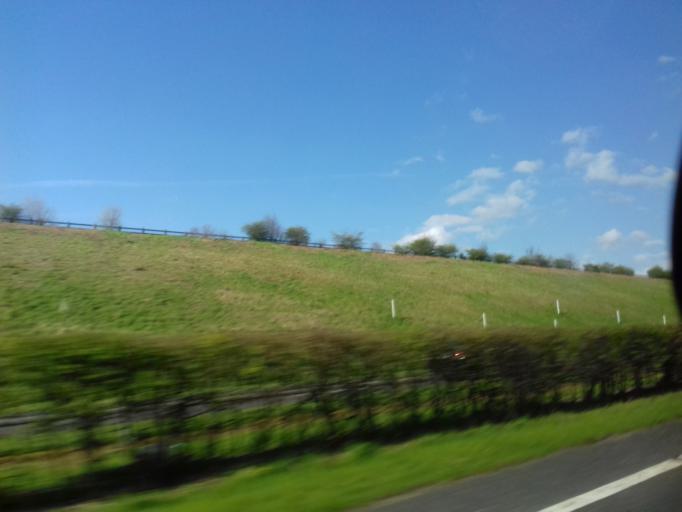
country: IE
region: Leinster
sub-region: Kildare
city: Kildare
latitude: 53.1539
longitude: -6.8789
